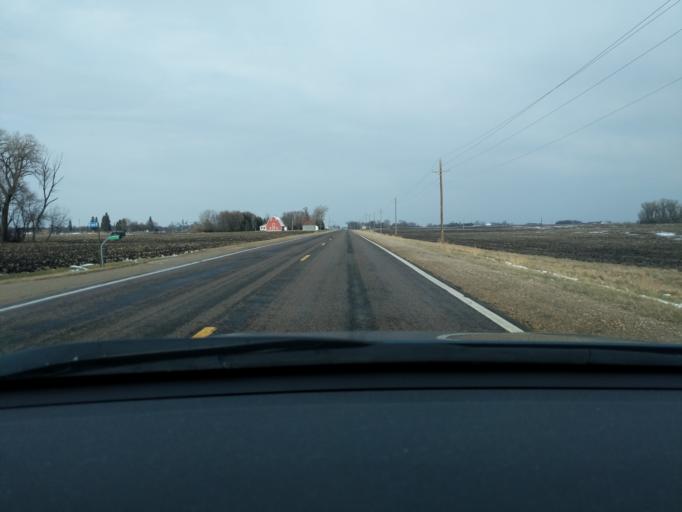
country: US
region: Minnesota
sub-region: Renville County
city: Renville
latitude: 44.7697
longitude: -95.3408
